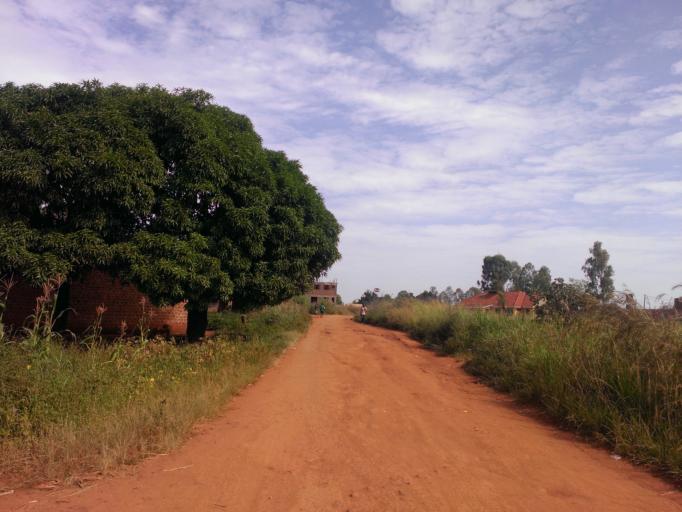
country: UG
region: Northern Region
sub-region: Gulu District
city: Gulu
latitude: 2.7848
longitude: 32.3179
